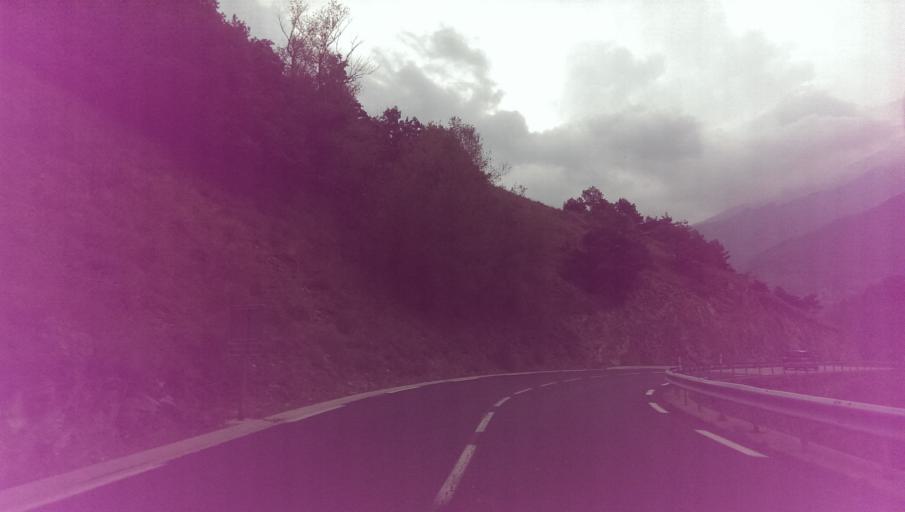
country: ES
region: Catalonia
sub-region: Provincia de Girona
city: Llivia
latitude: 42.5060
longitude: 2.1549
